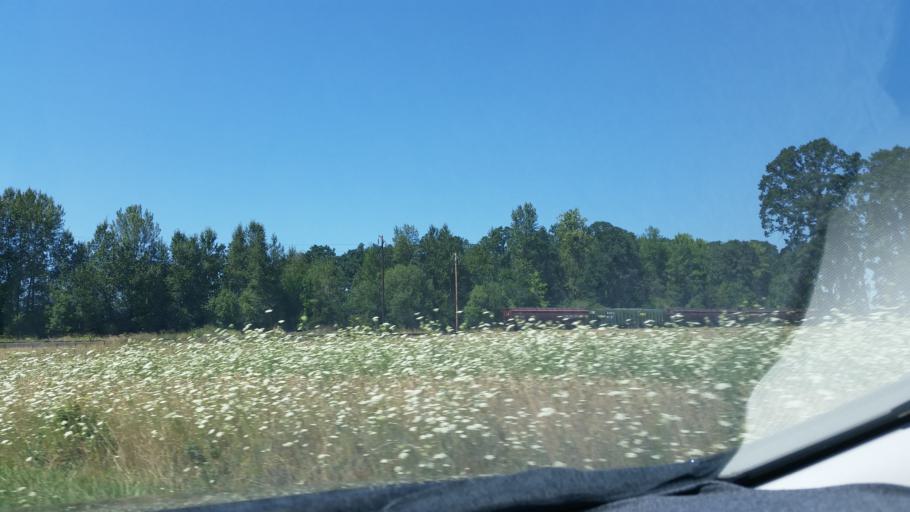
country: US
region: Oregon
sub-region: Clackamas County
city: Wilsonville
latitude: 45.2596
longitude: -122.8023
